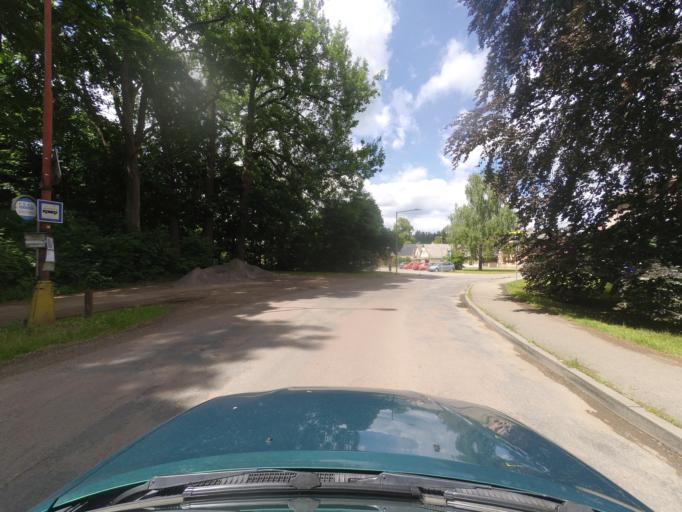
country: CZ
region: Pardubicky
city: Zamberk
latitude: 50.0869
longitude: 16.4679
